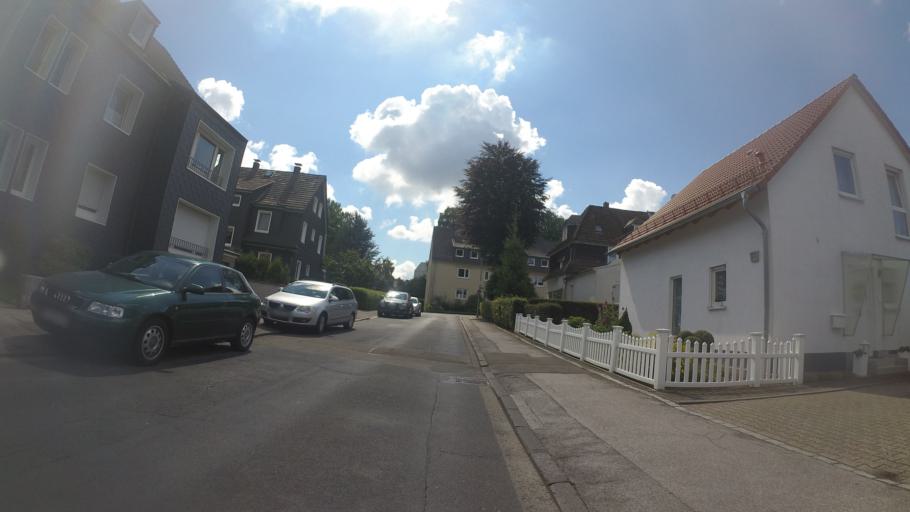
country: DE
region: North Rhine-Westphalia
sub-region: Regierungsbezirk Dusseldorf
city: Remscheid
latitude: 51.2091
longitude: 7.2447
